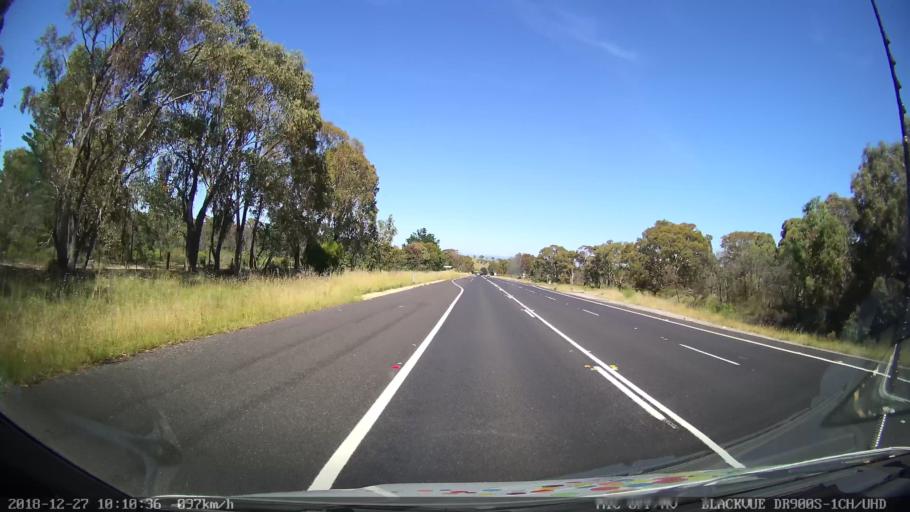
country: AU
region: New South Wales
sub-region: Bathurst Regional
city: Kelso
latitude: -33.4523
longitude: 149.7890
